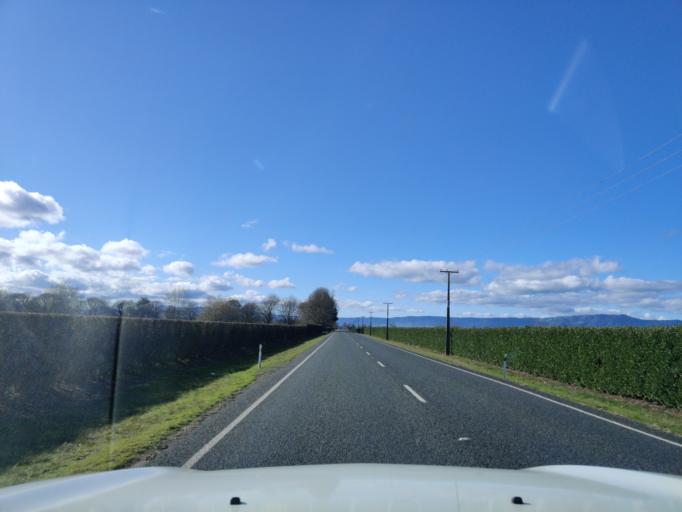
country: NZ
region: Waikato
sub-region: Matamata-Piako District
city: Matamata
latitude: -37.8774
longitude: 175.7391
